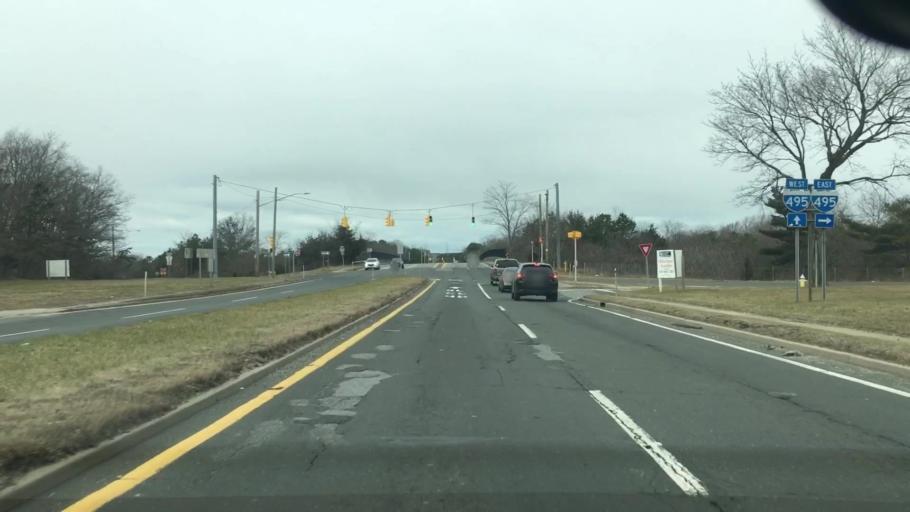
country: US
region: New York
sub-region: Suffolk County
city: Medford
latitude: 40.8214
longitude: -72.9727
